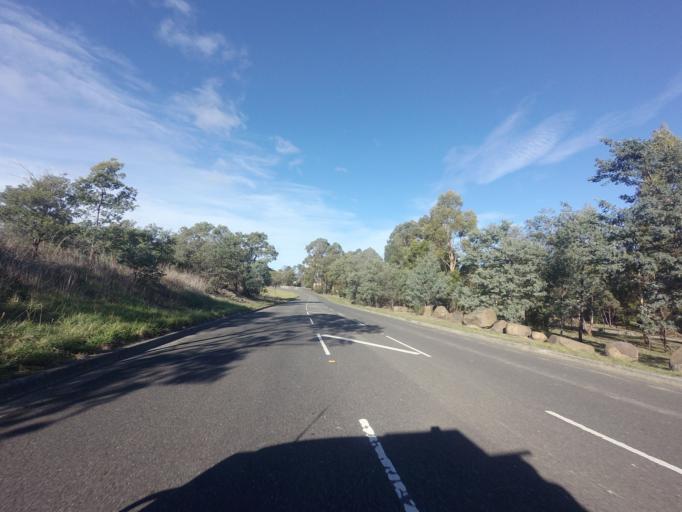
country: AU
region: Tasmania
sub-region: Clarence
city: Rokeby
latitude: -42.8879
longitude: 147.4377
